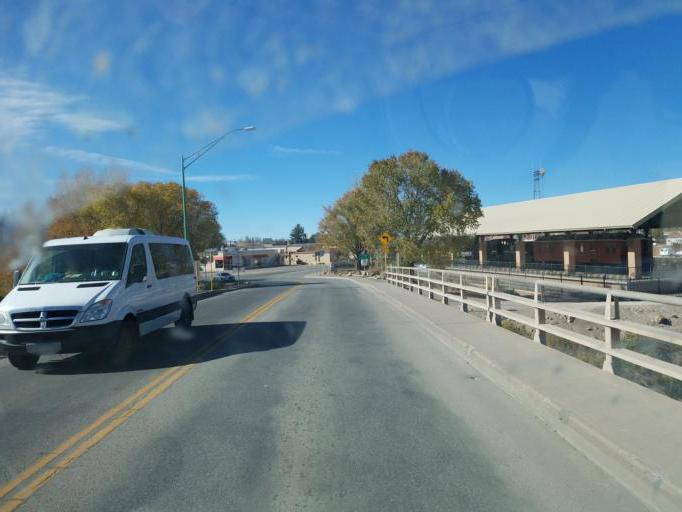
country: US
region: Colorado
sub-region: Alamosa County
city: Alamosa
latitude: 37.4699
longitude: -105.8614
